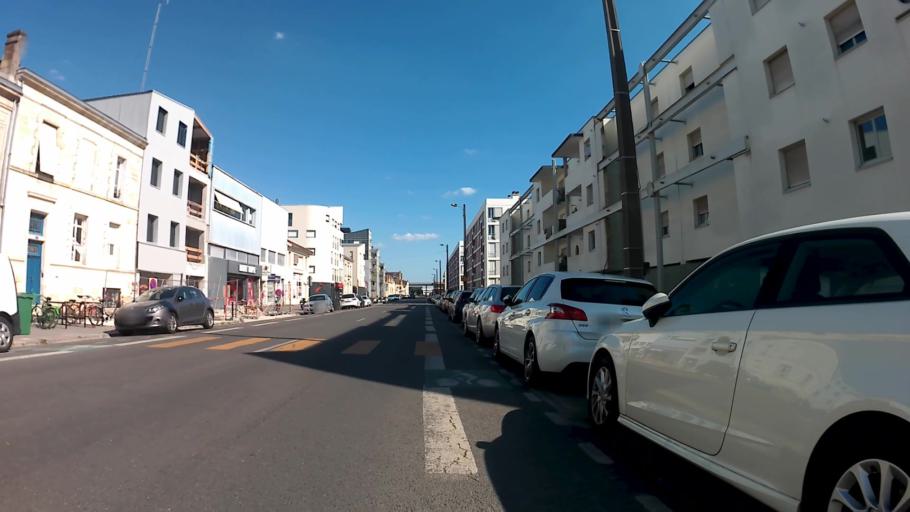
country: FR
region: Aquitaine
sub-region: Departement de la Gironde
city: Bordeaux
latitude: 44.8618
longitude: -0.5593
